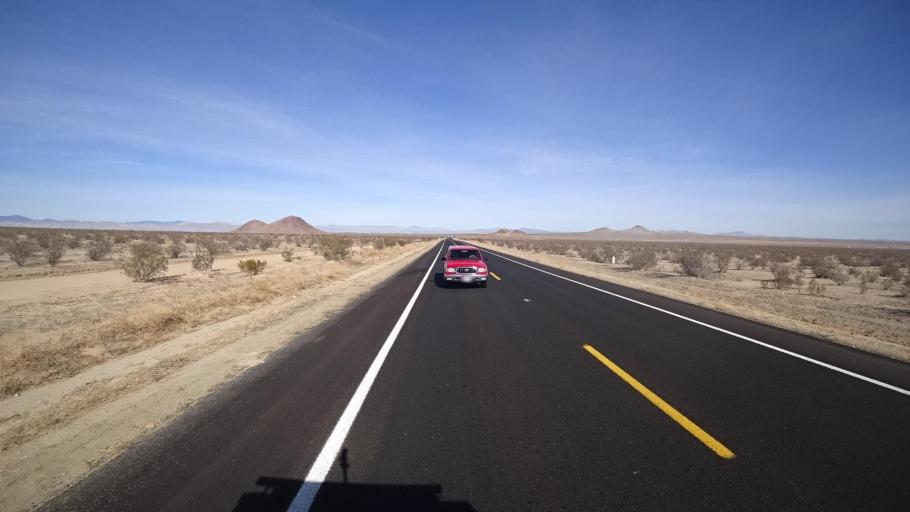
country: US
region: California
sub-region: Kern County
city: North Edwards
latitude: 35.0546
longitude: -117.9175
